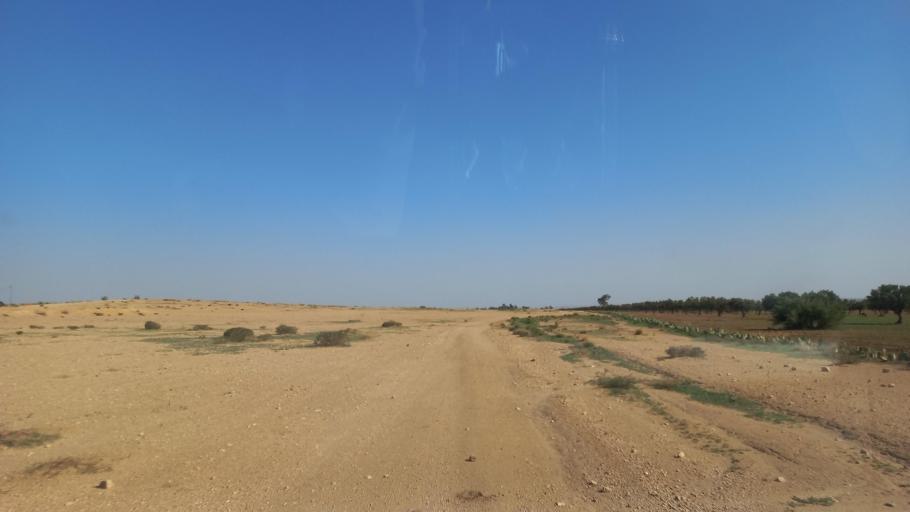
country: TN
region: Al Qasrayn
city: Kasserine
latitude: 35.3117
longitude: 9.0181
